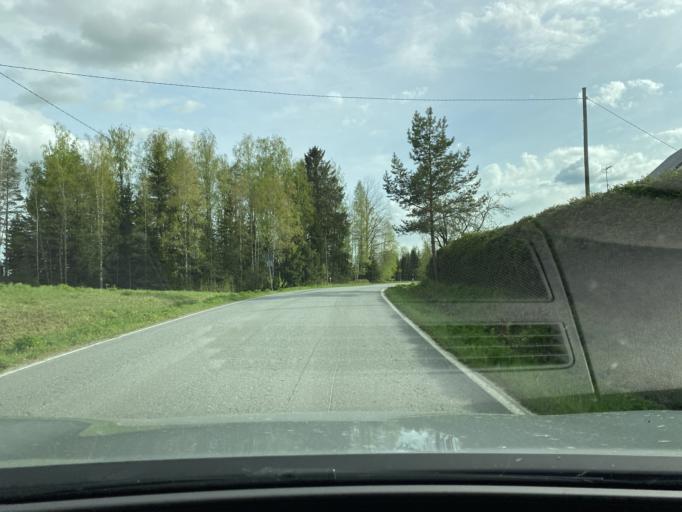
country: FI
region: Varsinais-Suomi
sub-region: Salo
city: Kiikala
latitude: 60.5226
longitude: 23.5427
